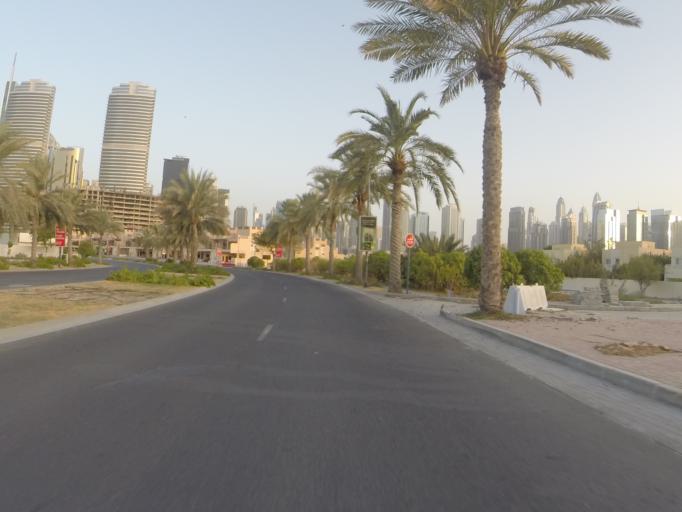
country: AE
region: Dubai
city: Dubai
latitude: 25.0670
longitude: 55.1503
